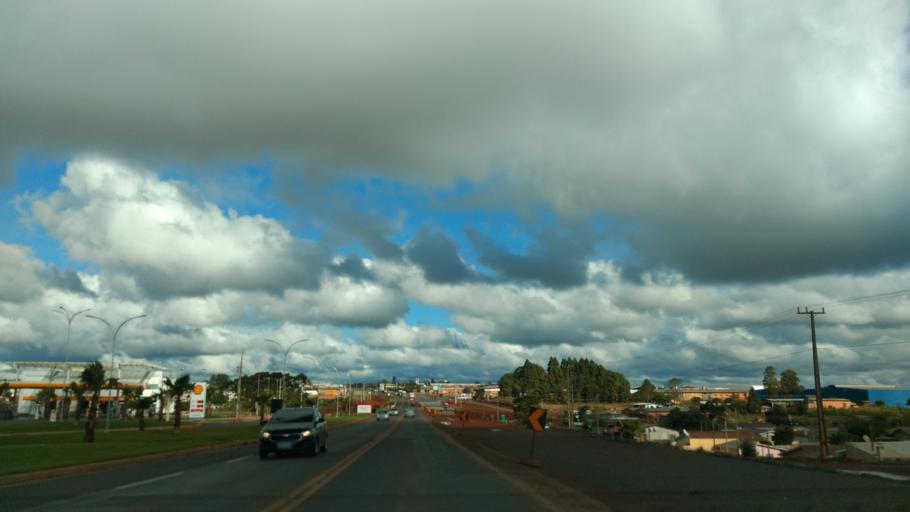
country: BR
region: Parana
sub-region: Guarapuava
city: Guarapuava
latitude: -25.3516
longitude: -51.4863
